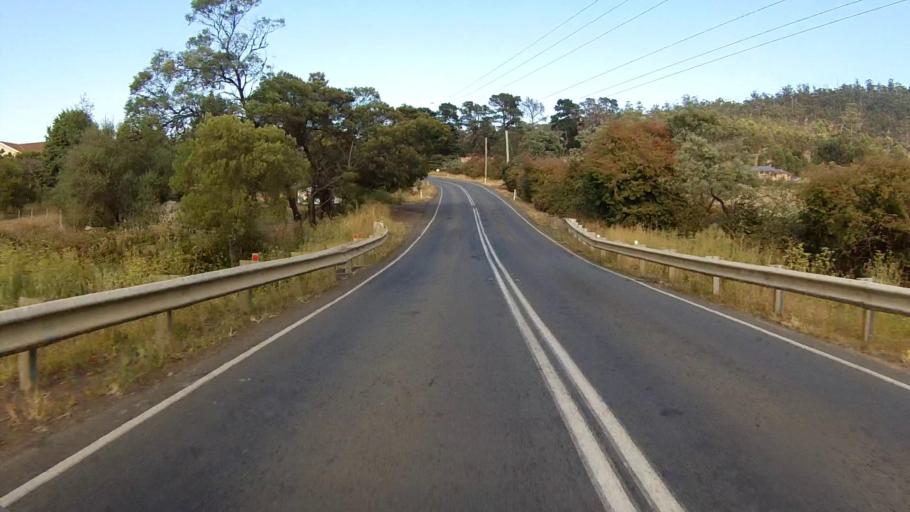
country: AU
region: Tasmania
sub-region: Brighton
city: Bridgewater
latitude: -42.7295
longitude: 147.1792
